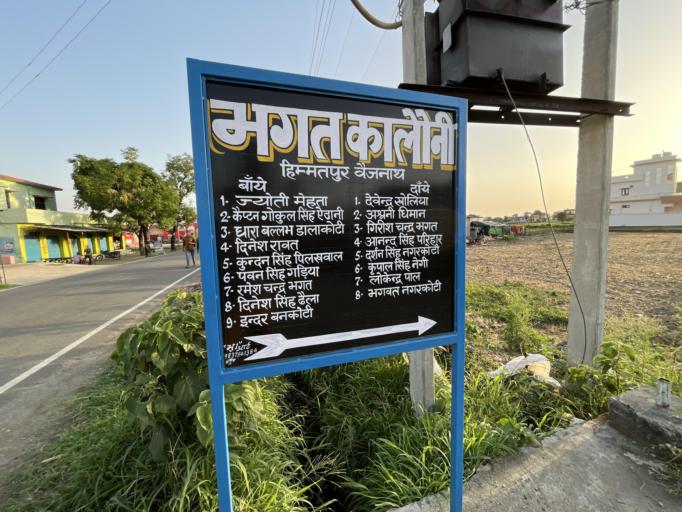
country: IN
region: Uttarakhand
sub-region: Naini Tal
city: Haldwani
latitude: 29.1840
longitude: 79.4754
